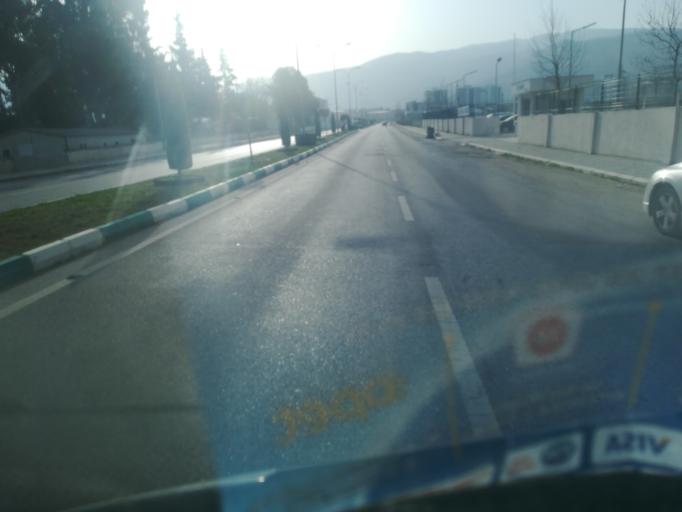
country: TR
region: Osmaniye
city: Osmaniye
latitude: 37.0581
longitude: 36.2178
